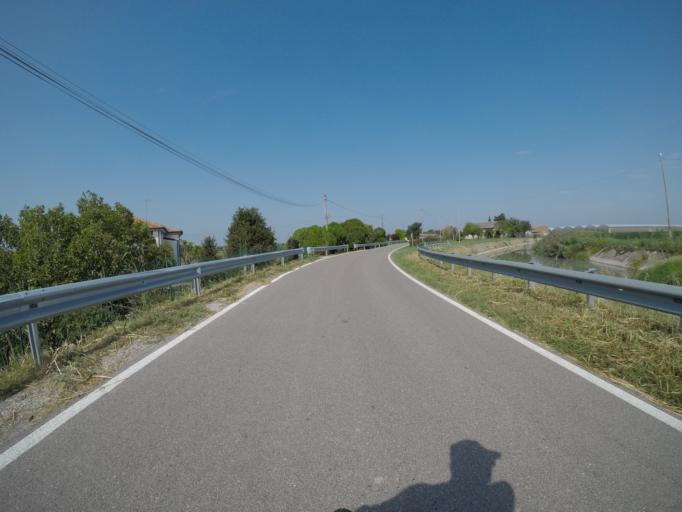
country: IT
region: Veneto
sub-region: Provincia di Rovigo
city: Lendinara
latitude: 45.0646
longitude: 11.6147
